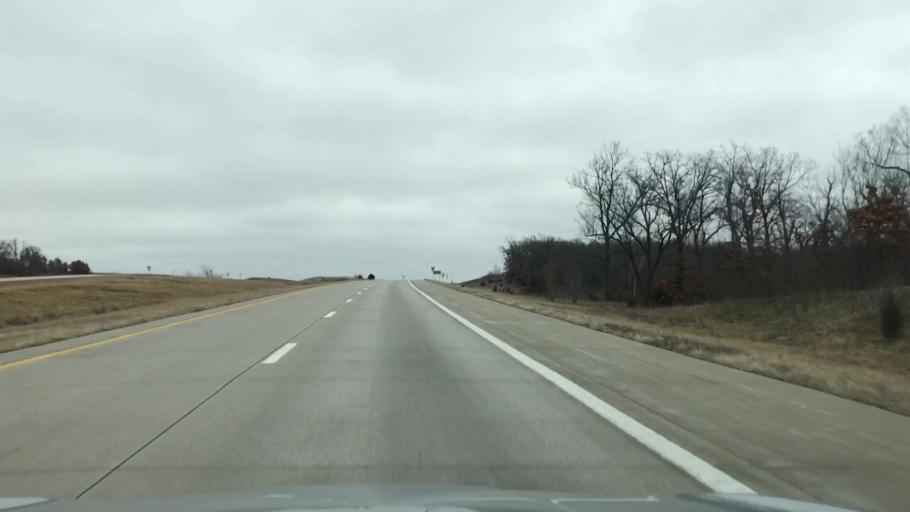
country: US
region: Missouri
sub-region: Linn County
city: Marceline
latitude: 39.7624
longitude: -92.7957
